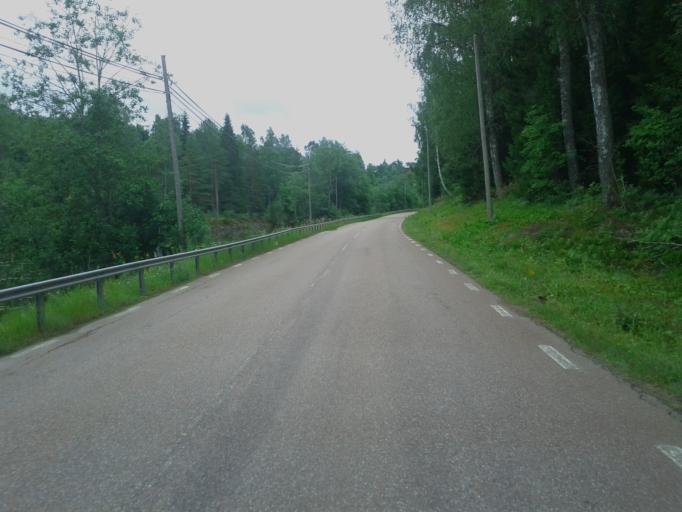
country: SE
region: Dalarna
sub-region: Smedjebackens Kommun
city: Smedjebacken
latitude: 60.3109
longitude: 15.3732
